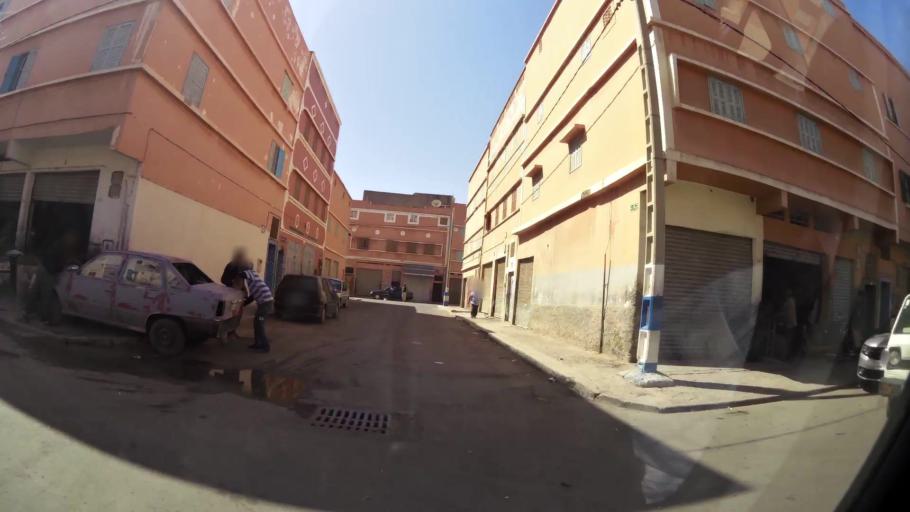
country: MA
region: Souss-Massa-Draa
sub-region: Inezgane-Ait Mellou
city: Inezgane
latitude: 30.3434
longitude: -9.5058
